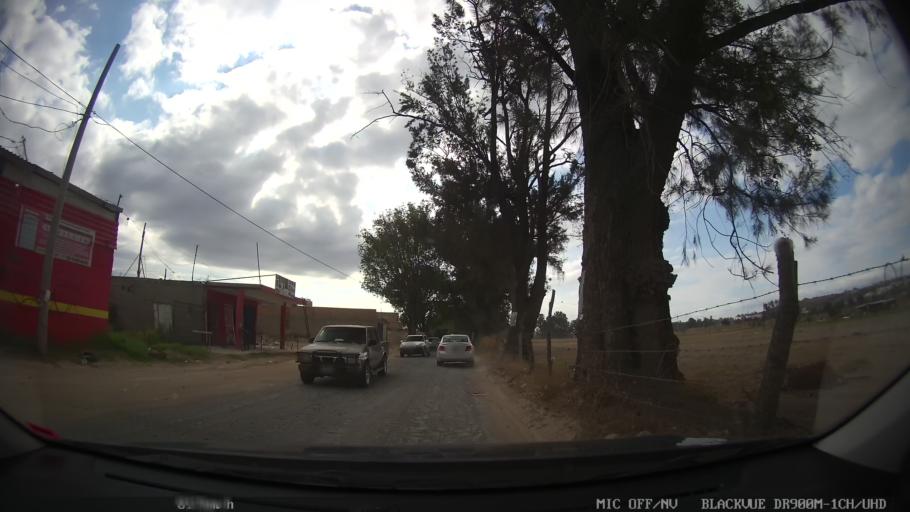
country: MX
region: Jalisco
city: Tonala
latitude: 20.6539
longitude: -103.2406
